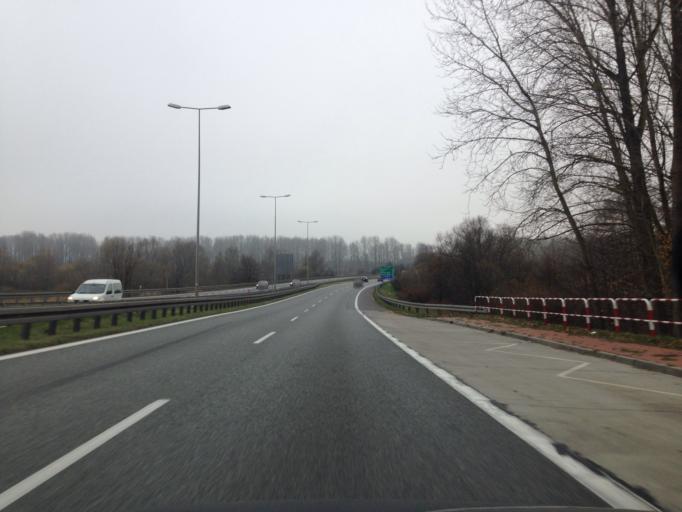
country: PL
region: Silesian Voivodeship
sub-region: Powiat bedzinski
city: Siewierz
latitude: 50.4541
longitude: 19.2296
